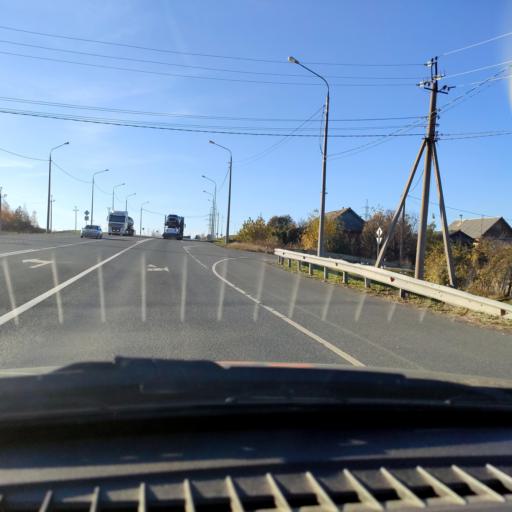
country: RU
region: Samara
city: Mezhdurechensk
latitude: 53.2485
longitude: 49.1690
